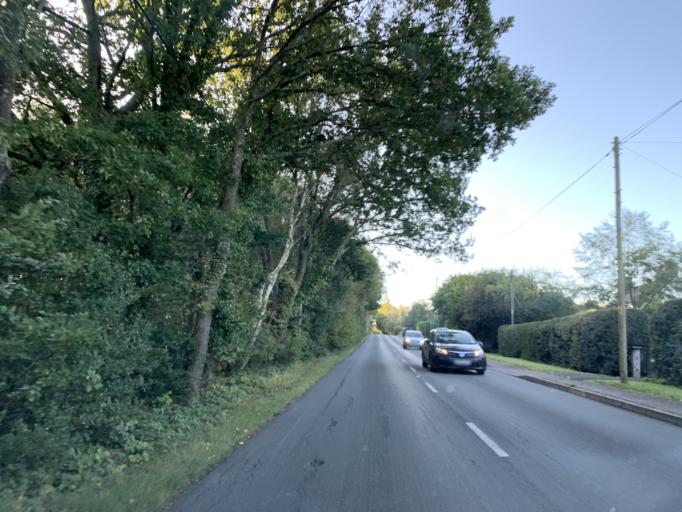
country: GB
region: England
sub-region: Wiltshire
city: Whiteparish
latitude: 50.9673
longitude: -1.6347
